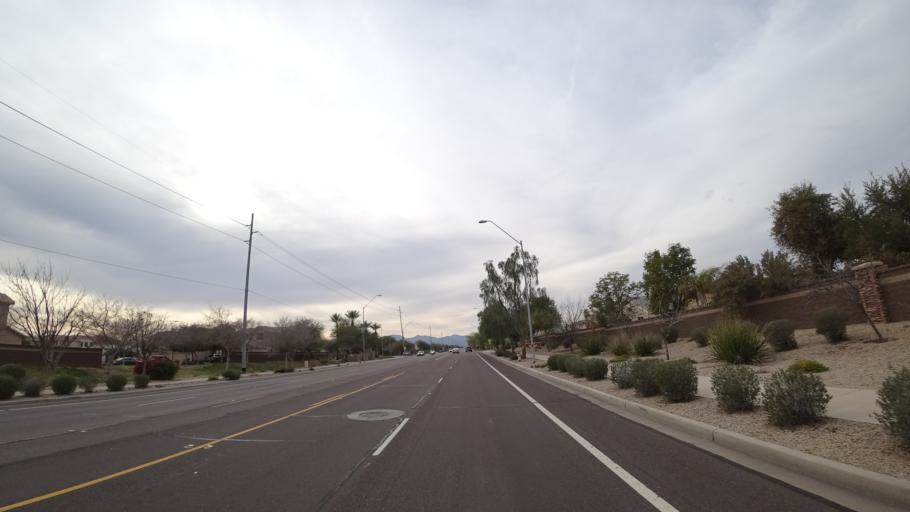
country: US
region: Arizona
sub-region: Maricopa County
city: Surprise
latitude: 33.5950
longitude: -112.3837
